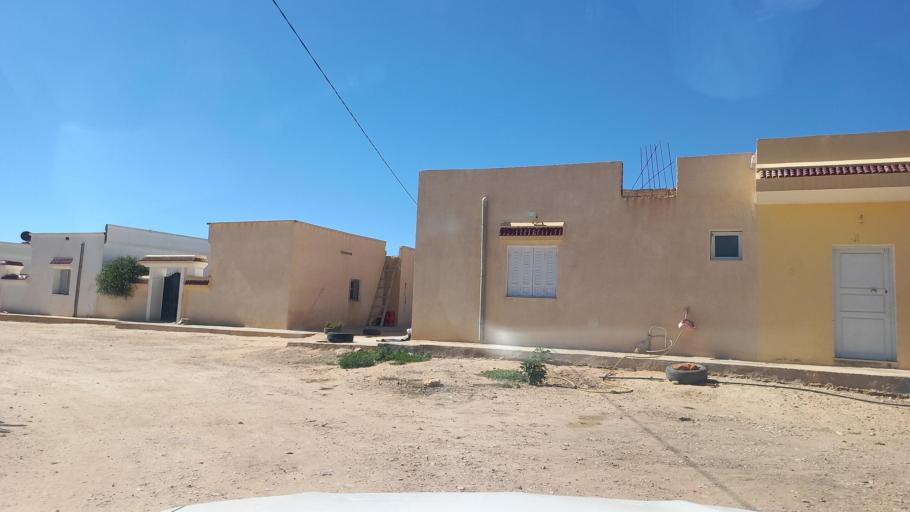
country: TN
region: Al Qasrayn
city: Sbiba
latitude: 35.3790
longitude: 9.0732
